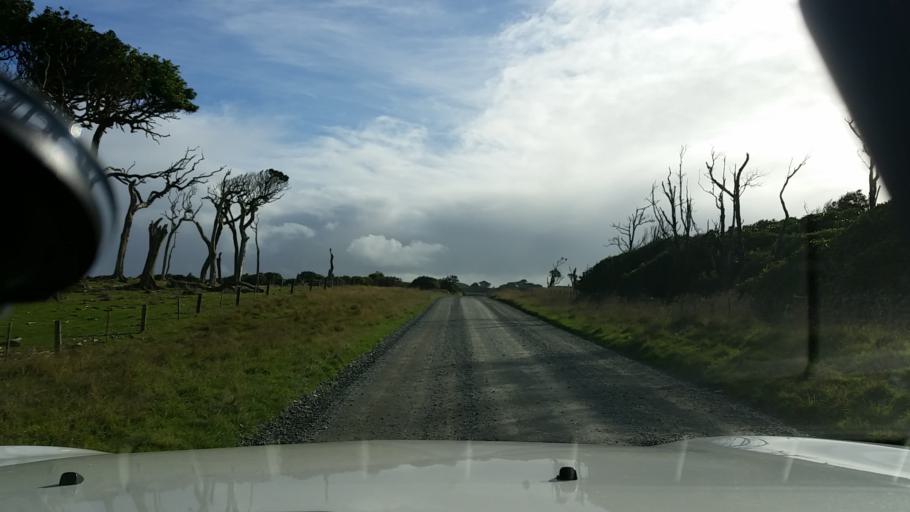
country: NZ
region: Chatham Islands
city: Waitangi
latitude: -43.8210
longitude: -176.5706
